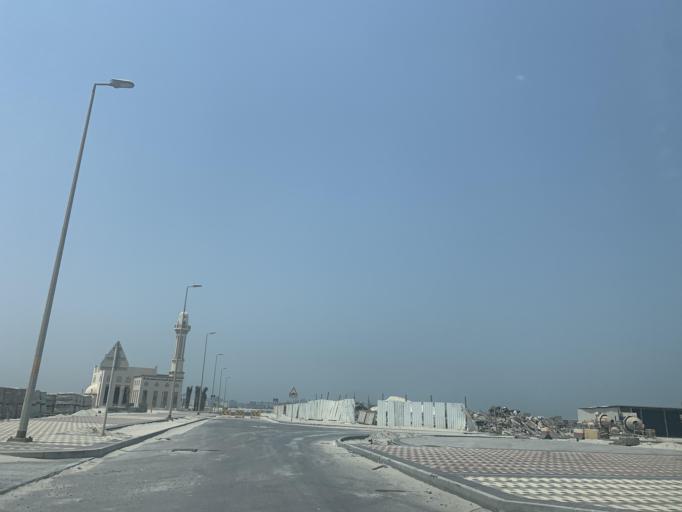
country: BH
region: Muharraq
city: Al Hadd
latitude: 26.2425
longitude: 50.6673
